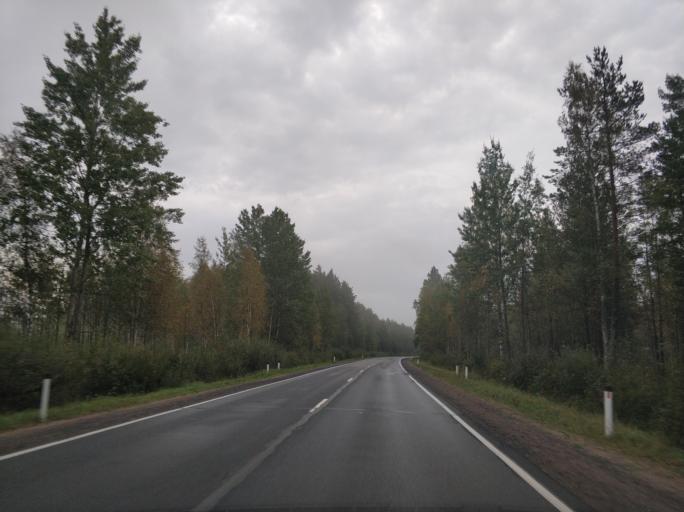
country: RU
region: Leningrad
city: Shcheglovo
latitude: 60.1002
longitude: 30.8337
